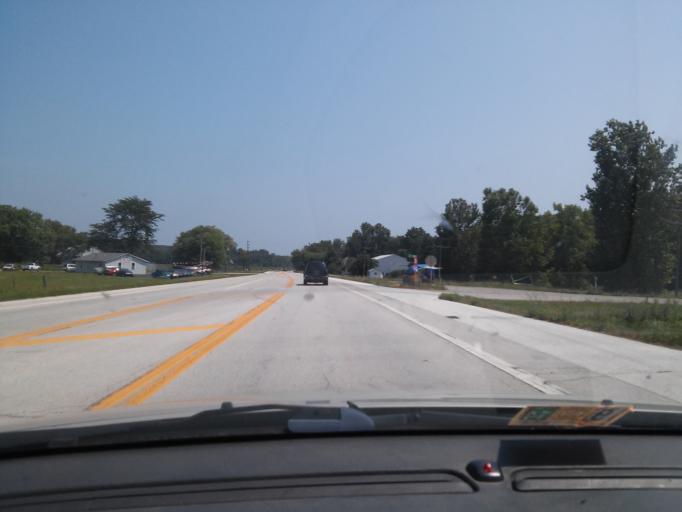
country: US
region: Missouri
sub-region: Pike County
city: Bowling Green
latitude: 39.3650
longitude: -91.1789
